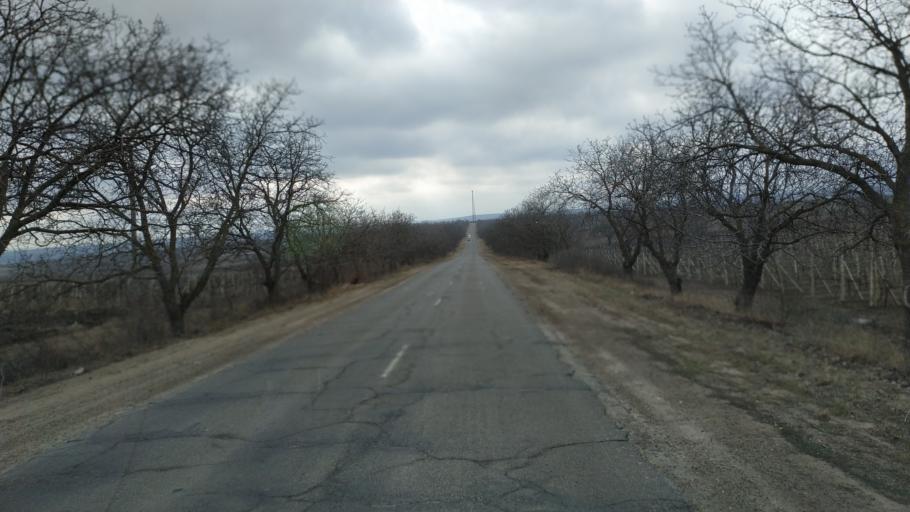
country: MD
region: Laloveni
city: Ialoveni
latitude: 46.8982
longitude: 28.7730
